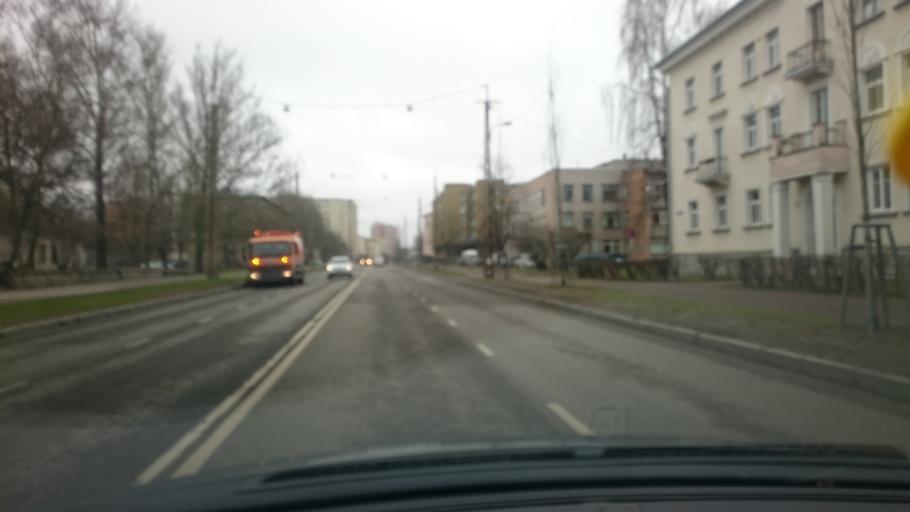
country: EE
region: Harju
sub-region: Tallinna linn
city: Tallinn
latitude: 59.4511
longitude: 24.6952
